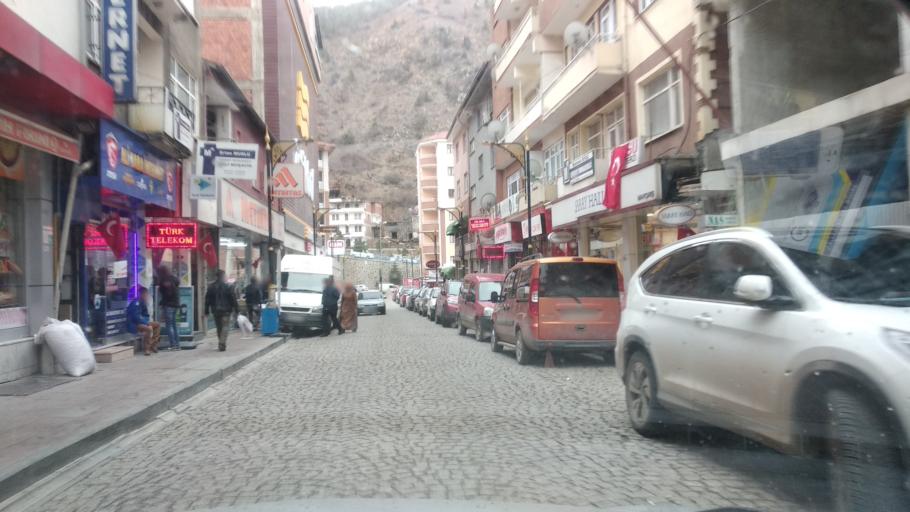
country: TR
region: Gumushane
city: Gumushkhane
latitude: 40.4587
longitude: 39.4807
